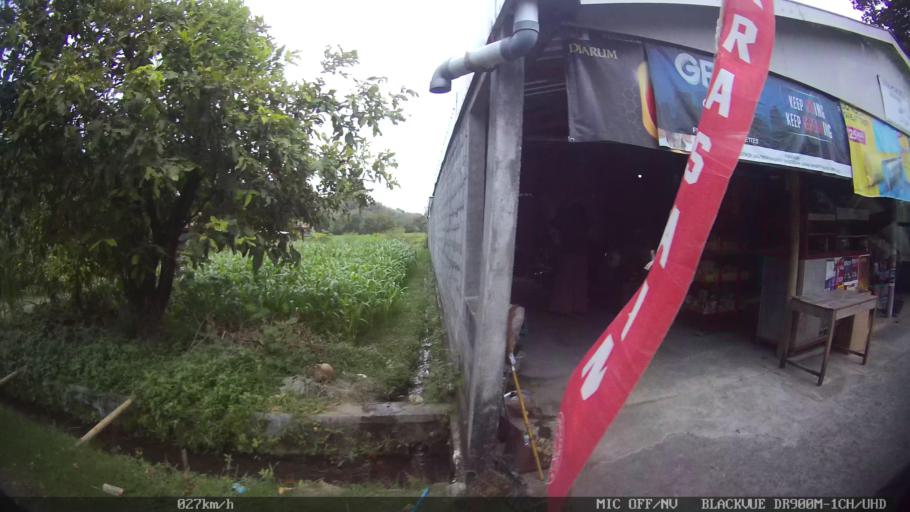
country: ID
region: Daerah Istimewa Yogyakarta
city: Depok
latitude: -7.8200
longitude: 110.4645
